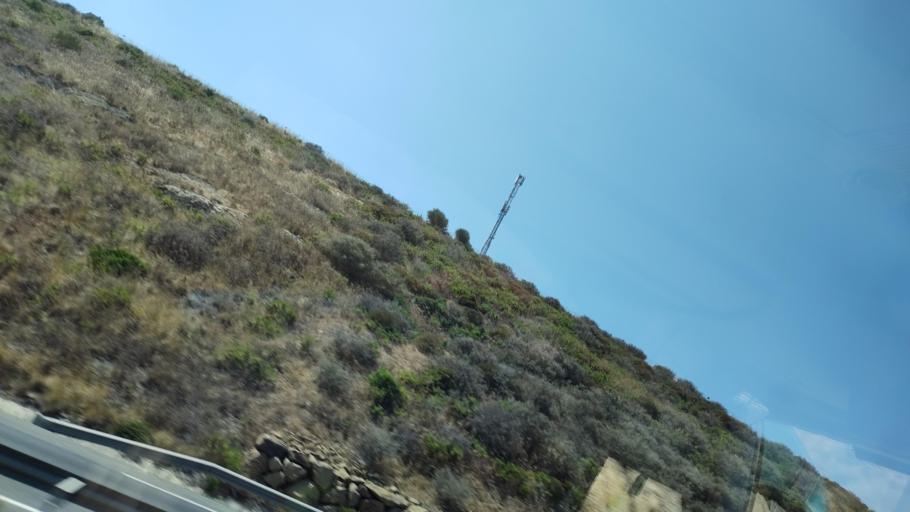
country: ES
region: Andalusia
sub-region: Provincia de Malaga
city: Manilva
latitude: 36.3252
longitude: -5.2651
